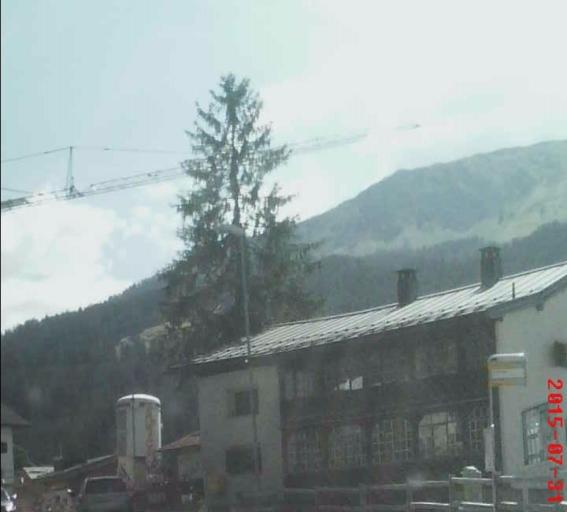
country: CH
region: Grisons
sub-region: Praettigau/Davos District
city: Klosters Serneus
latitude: 46.8785
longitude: 9.8799
